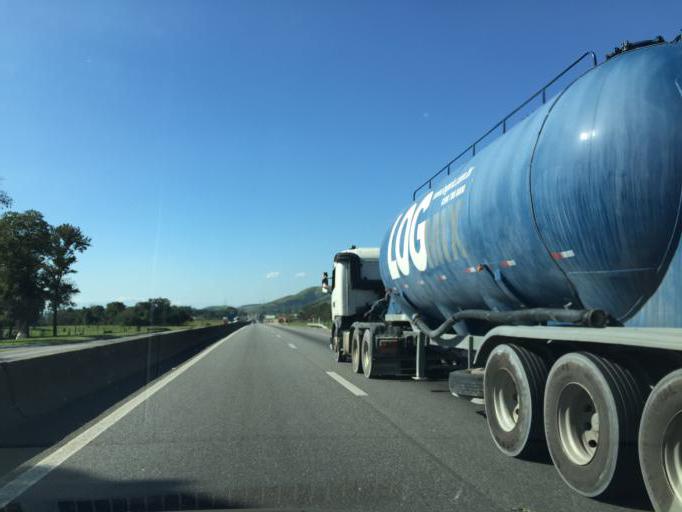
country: BR
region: Sao Paulo
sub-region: Aparecida
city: Aparecida
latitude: -22.8994
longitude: -45.3023
